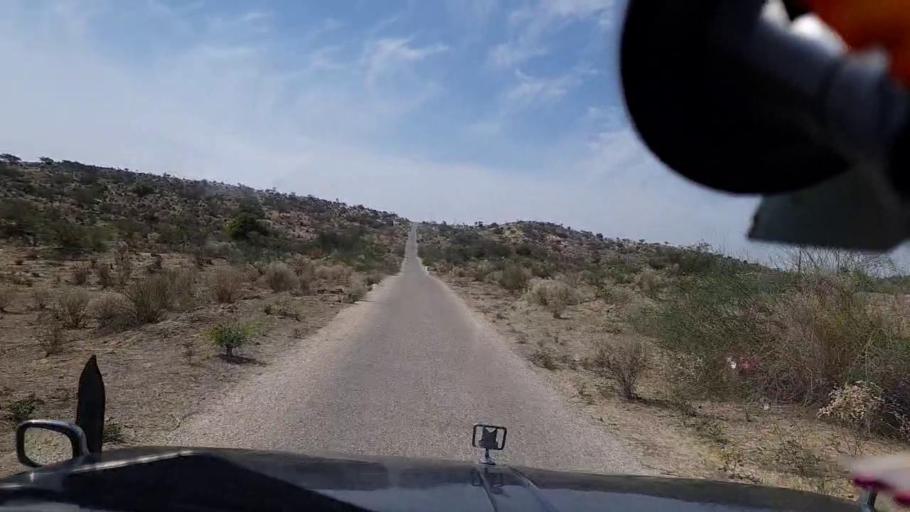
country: PK
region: Sindh
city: Diplo
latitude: 24.3879
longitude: 69.5881
